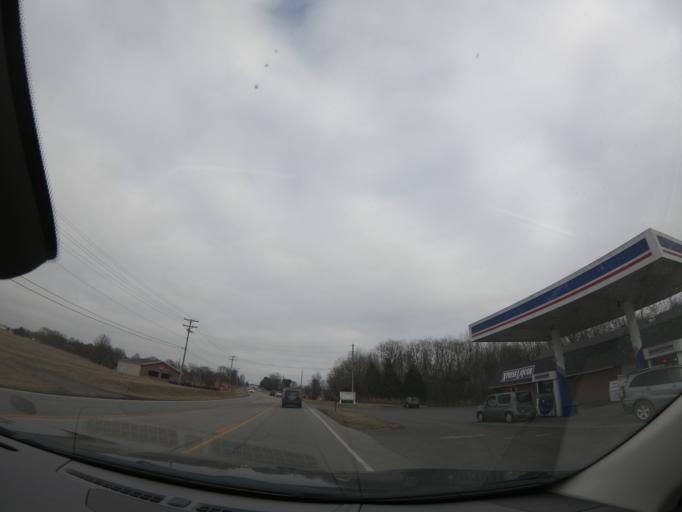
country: US
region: Kentucky
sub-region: Nelson County
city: Bardstown
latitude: 37.8250
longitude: -85.4366
